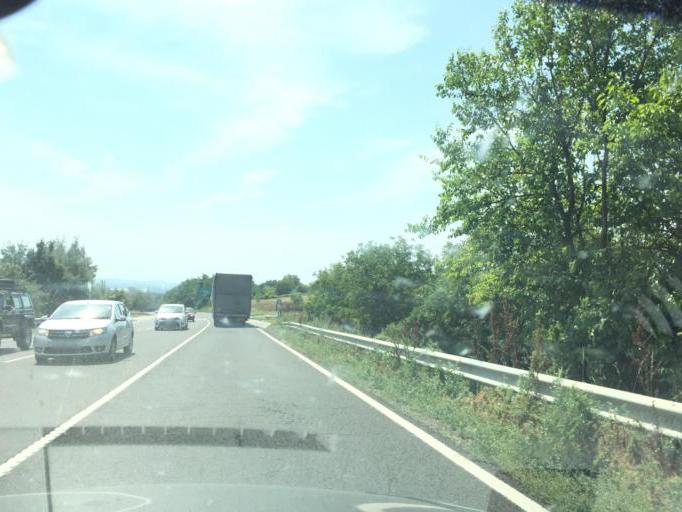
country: HU
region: Pest
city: Veroce
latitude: 47.8212
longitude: 19.0894
